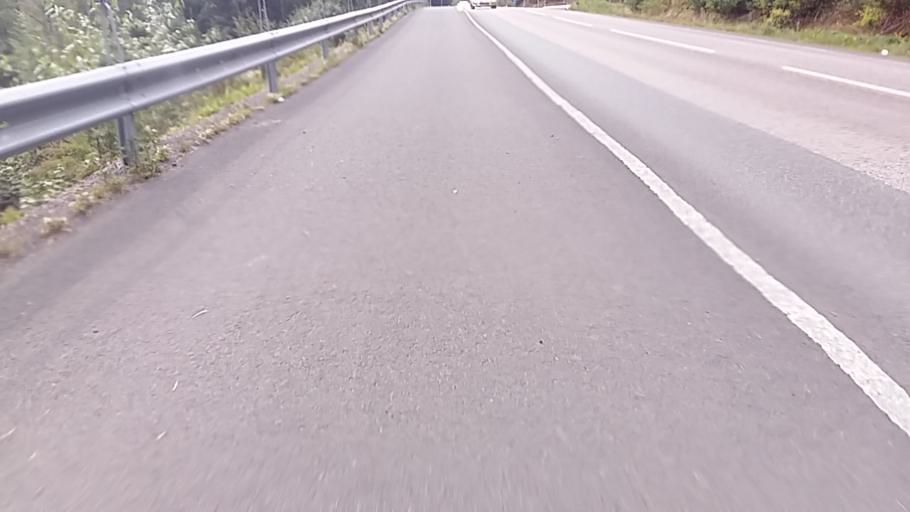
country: SE
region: Joenkoeping
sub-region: Jonkopings Kommun
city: Odensjo
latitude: 57.7162
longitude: 14.1263
